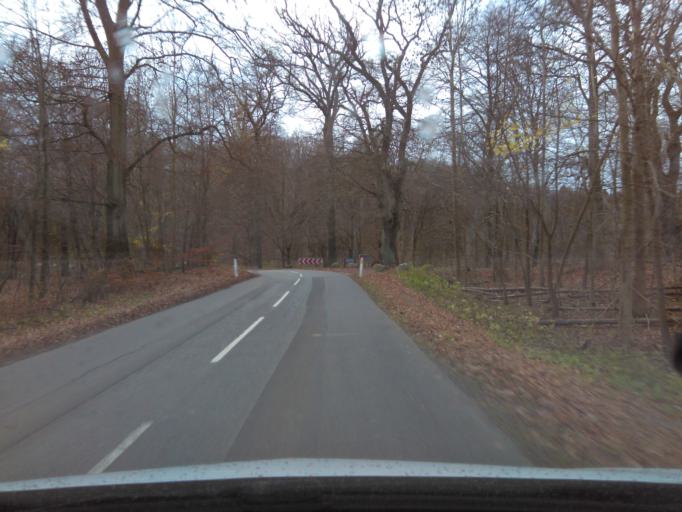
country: DK
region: Capital Region
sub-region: Fureso Kommune
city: Vaerlose
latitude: 55.7616
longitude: 12.3814
